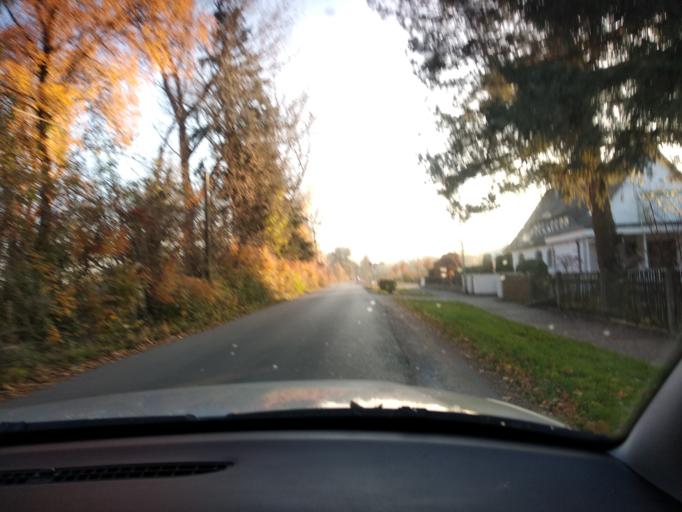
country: DE
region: Bavaria
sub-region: Upper Bavaria
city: Bogenhausen
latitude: 48.1447
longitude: 11.6549
